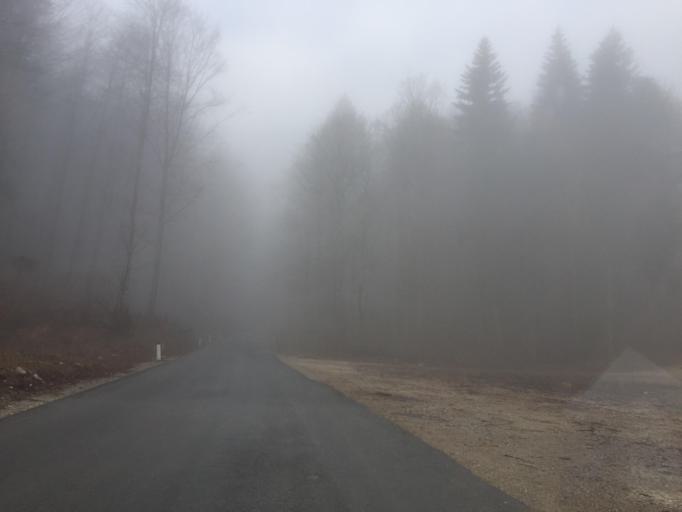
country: SI
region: Ajdovscina
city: Lokavec
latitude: 45.9551
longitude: 13.8599
